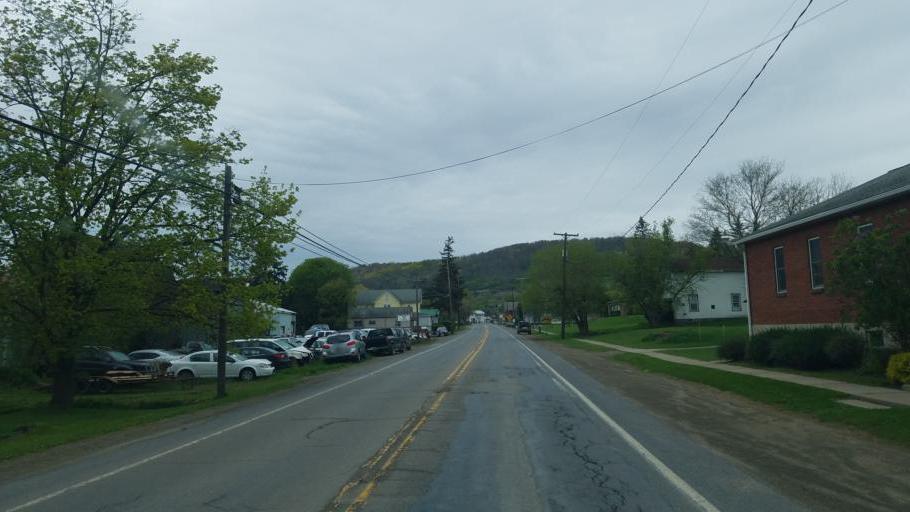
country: US
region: Pennsylvania
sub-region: Tioga County
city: Westfield
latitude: 41.9394
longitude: -77.6462
